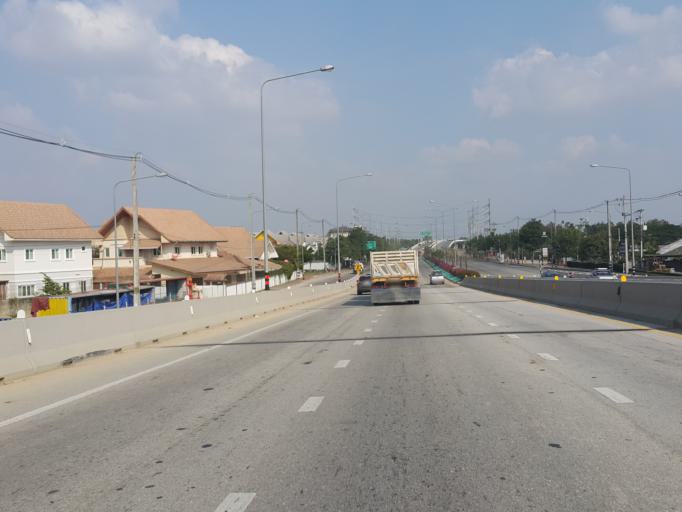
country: TH
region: Chiang Mai
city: Saraphi
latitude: 18.7504
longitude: 99.0259
